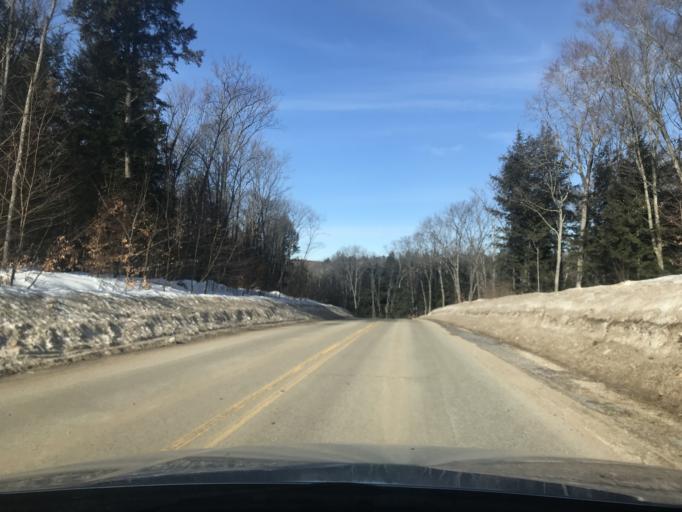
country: US
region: Michigan
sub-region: Dickinson County
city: Kingsford
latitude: 45.4095
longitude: -88.3526
